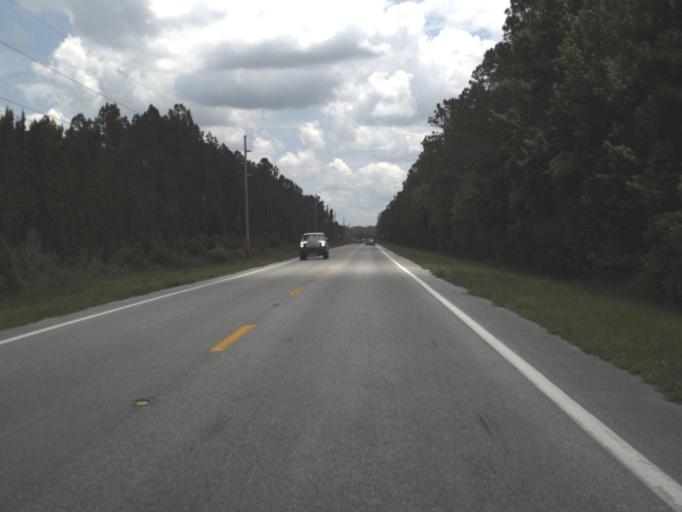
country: US
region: Florida
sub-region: Levy County
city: Bronson
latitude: 29.3305
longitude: -82.7632
